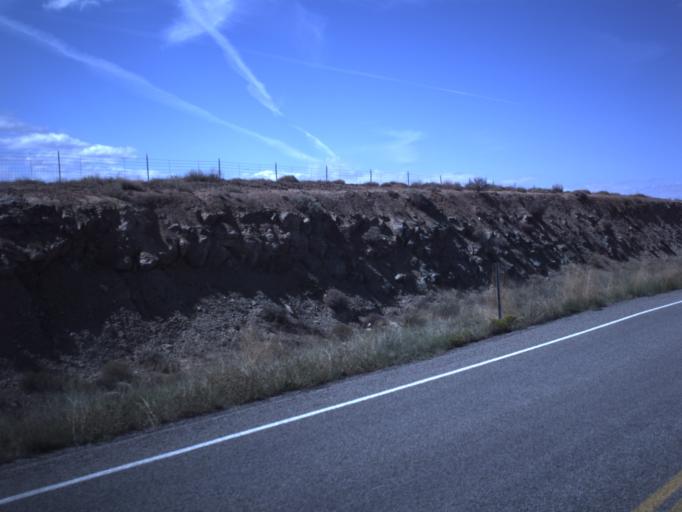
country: US
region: Colorado
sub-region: Montezuma County
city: Towaoc
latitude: 37.1752
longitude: -109.1046
